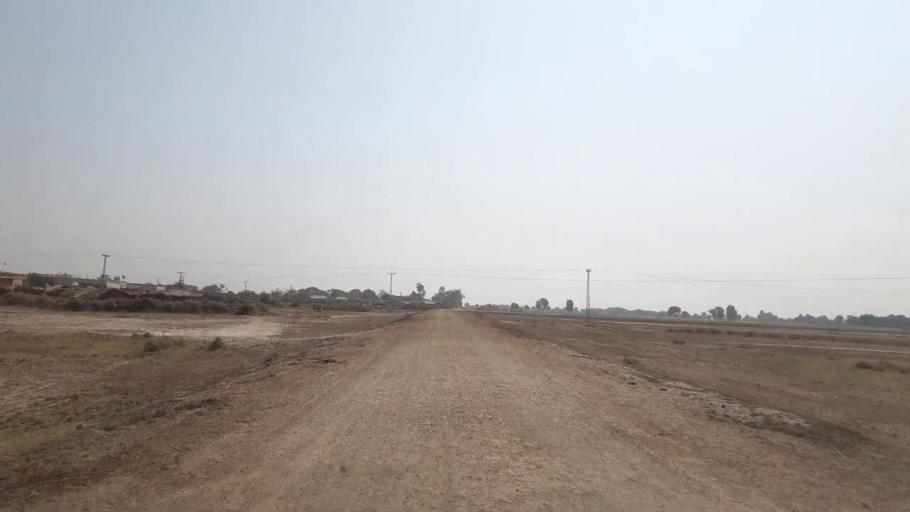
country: PK
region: Sindh
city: Mirpur Khas
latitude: 25.6404
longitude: 69.1460
